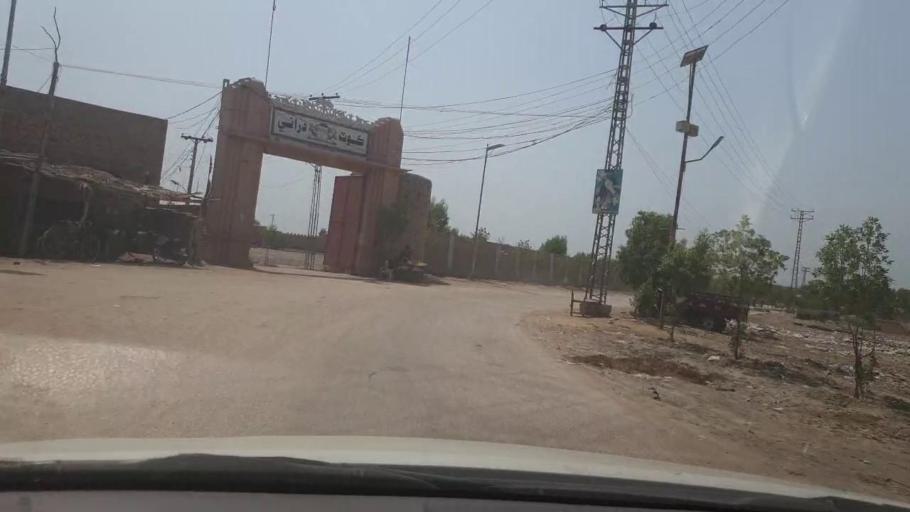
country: PK
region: Sindh
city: Garhi Yasin
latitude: 27.9096
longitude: 68.5132
